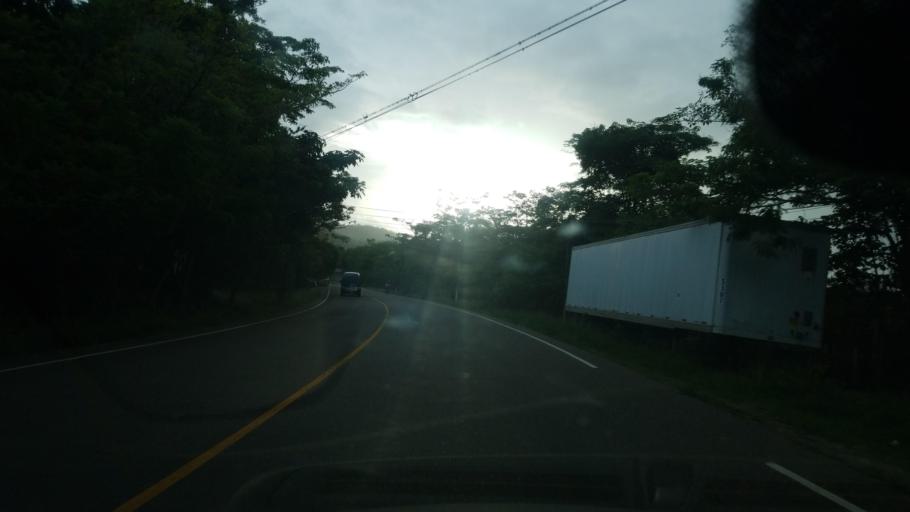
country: HN
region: Ocotepeque
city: Sinuapa
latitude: 14.5165
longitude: -89.2348
